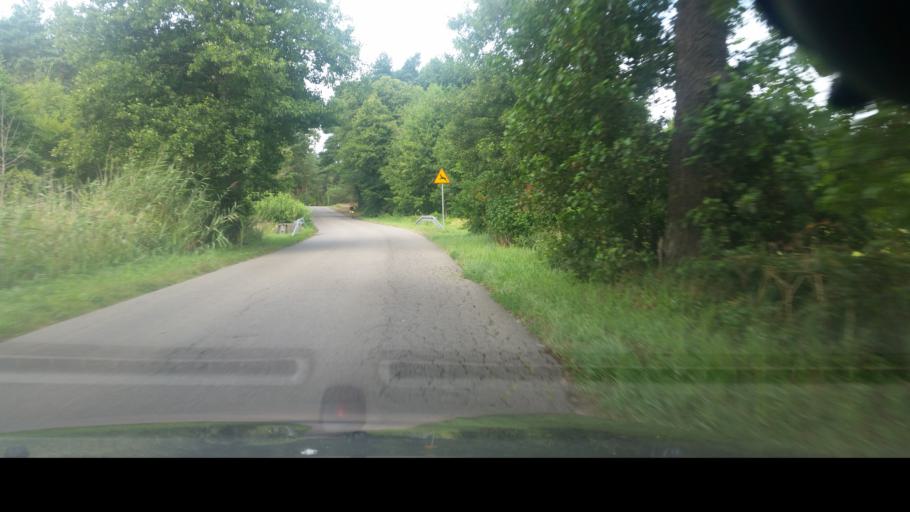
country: PL
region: Pomeranian Voivodeship
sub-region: Powiat leborski
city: Leba
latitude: 54.7382
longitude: 17.5969
